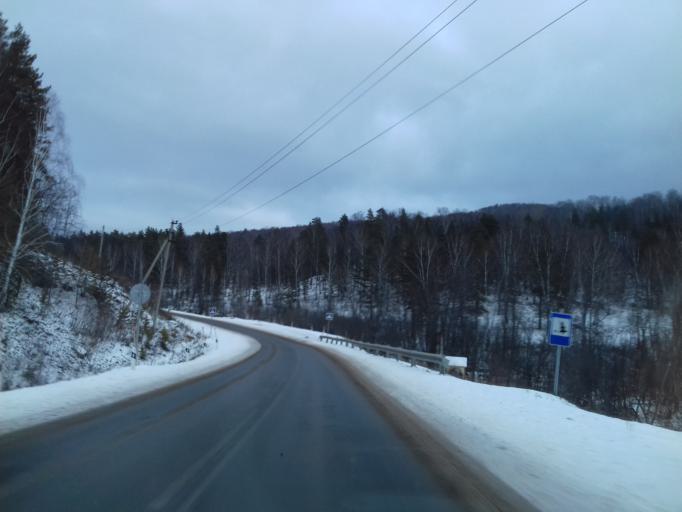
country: RU
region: Bashkortostan
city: Starosubkhangulovo
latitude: 53.1741
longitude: 57.4224
